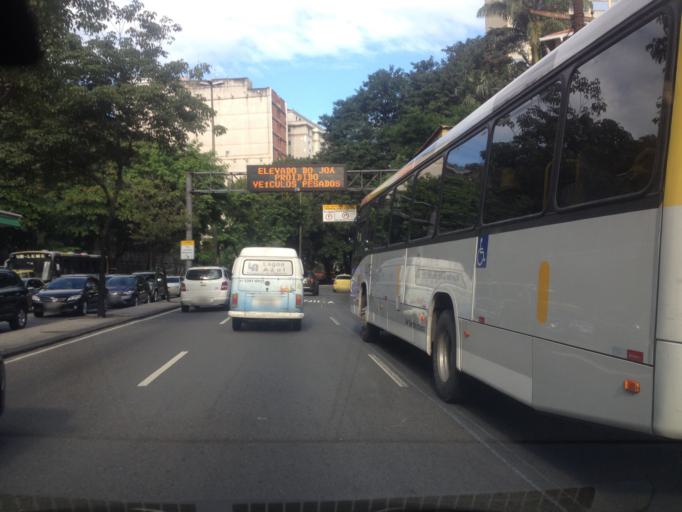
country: BR
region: Rio de Janeiro
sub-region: Rio De Janeiro
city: Rio de Janeiro
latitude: -22.9583
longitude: -43.1997
